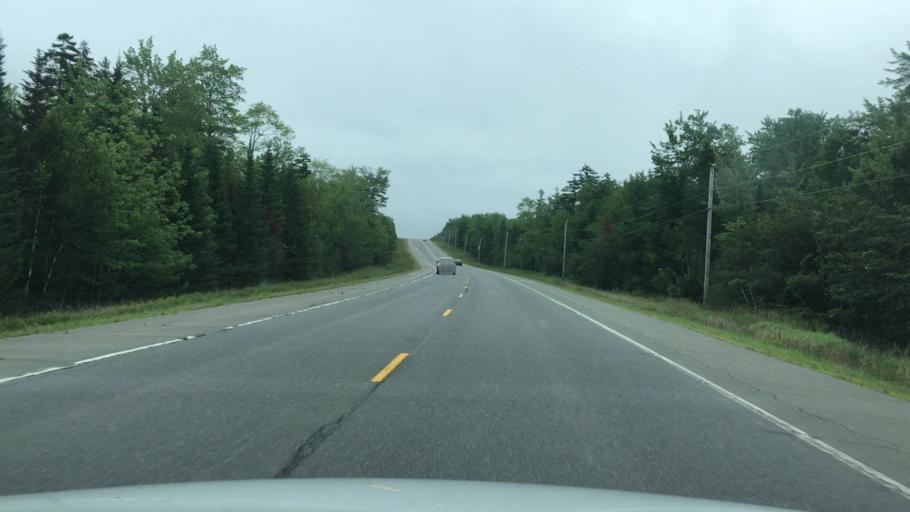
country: US
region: Maine
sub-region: Hancock County
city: Franklin
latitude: 44.8300
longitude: -68.1311
